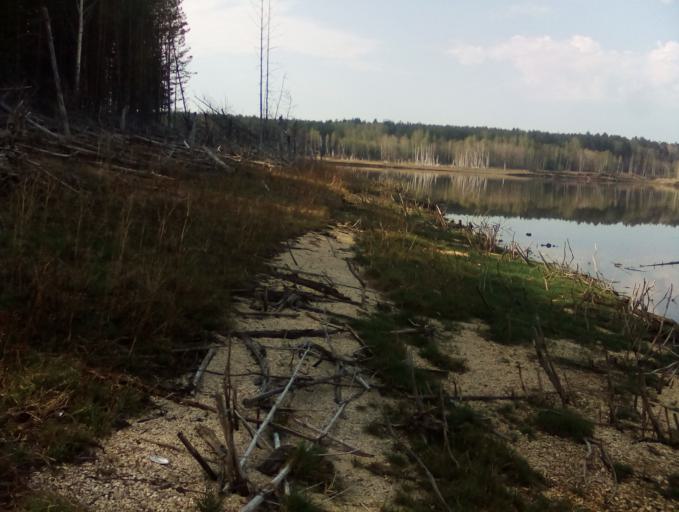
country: RU
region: Chelyabinsk
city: Nizhniy Ufaley
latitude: 55.7549
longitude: 60.1269
